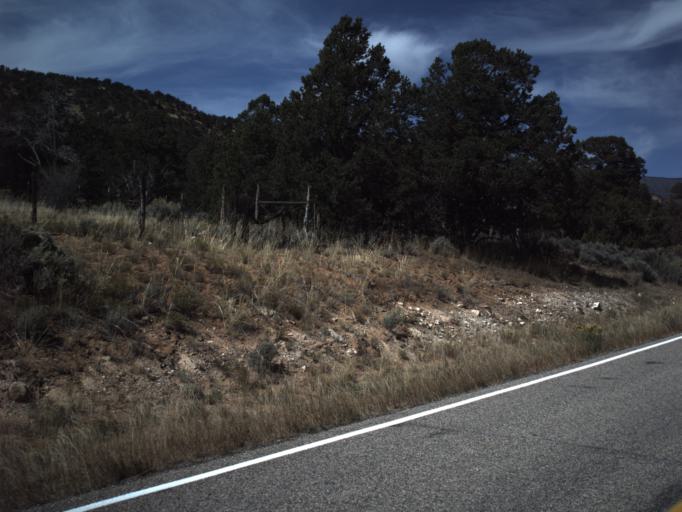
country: US
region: Utah
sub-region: Wayne County
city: Loa
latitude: 37.9215
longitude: -111.4252
